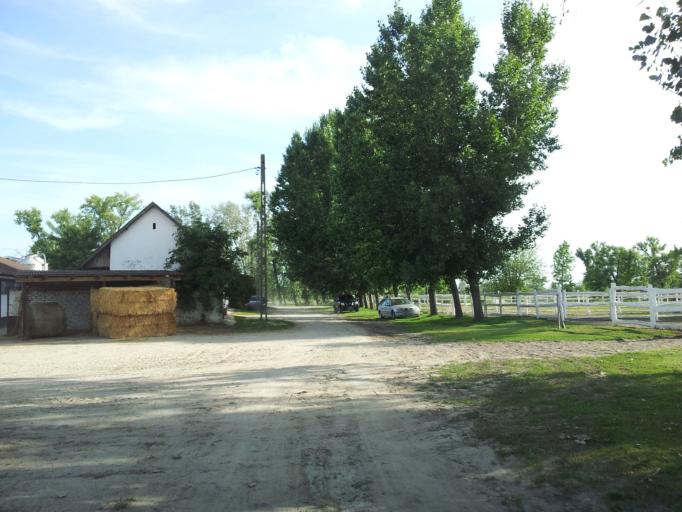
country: HU
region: Pest
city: Kiskunlachaza
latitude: 47.1948
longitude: 19.0015
